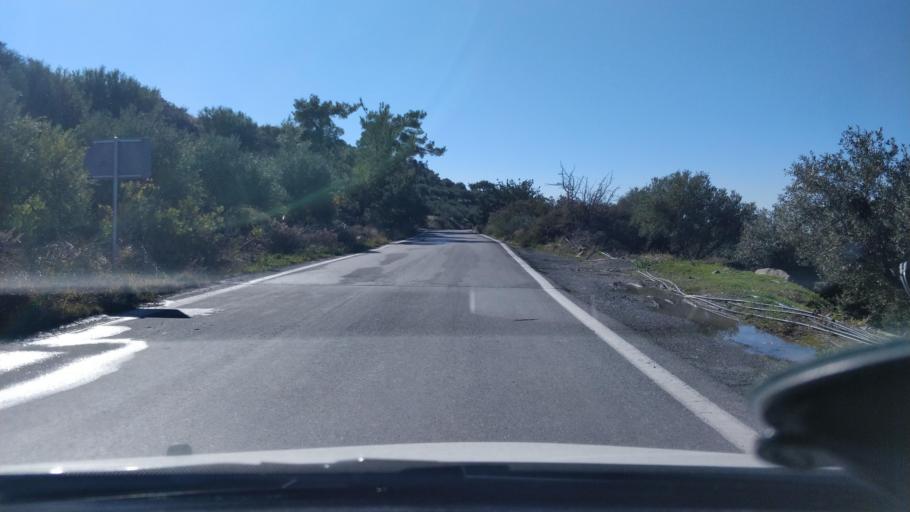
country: GR
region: Crete
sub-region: Nomos Irakleiou
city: Kastelli
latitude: 35.0182
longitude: 25.4493
